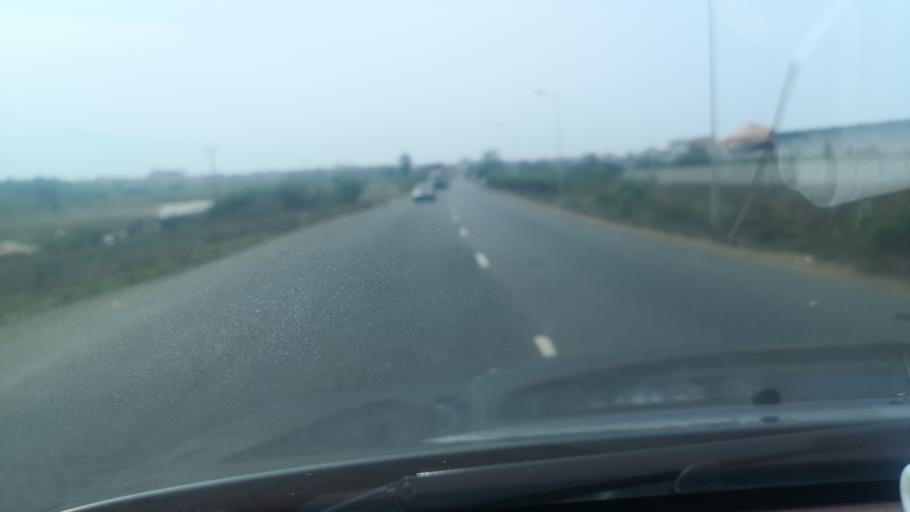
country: GH
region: Greater Accra
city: Nungua
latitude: 5.6113
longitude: -0.0539
